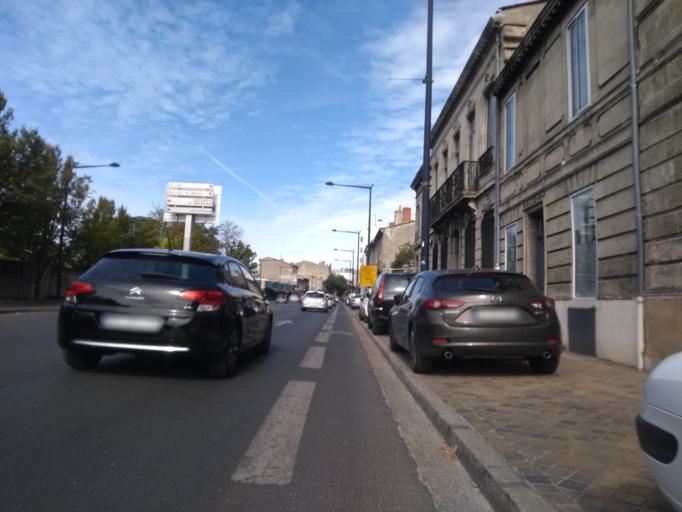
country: FR
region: Aquitaine
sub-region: Departement de la Gironde
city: Bordeaux
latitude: 44.8471
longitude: -0.5979
